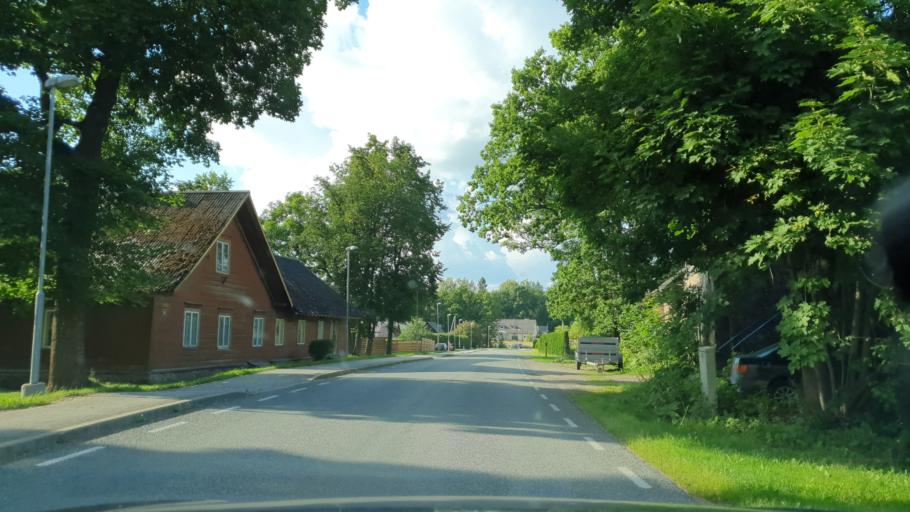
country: EE
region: Jogevamaa
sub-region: Tabivere vald
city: Tabivere
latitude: 58.6806
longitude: 26.5860
